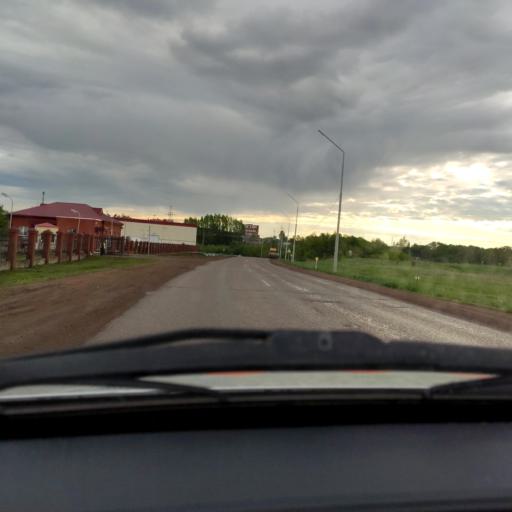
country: RU
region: Bashkortostan
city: Mikhaylovka
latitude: 54.8325
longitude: 55.8177
